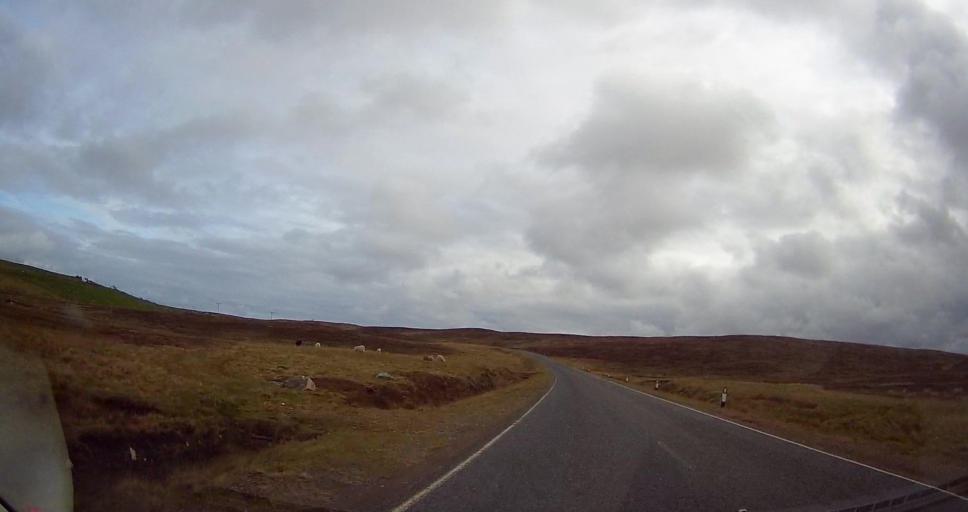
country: GB
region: Scotland
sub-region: Shetland Islands
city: Shetland
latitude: 60.5697
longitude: -1.1747
